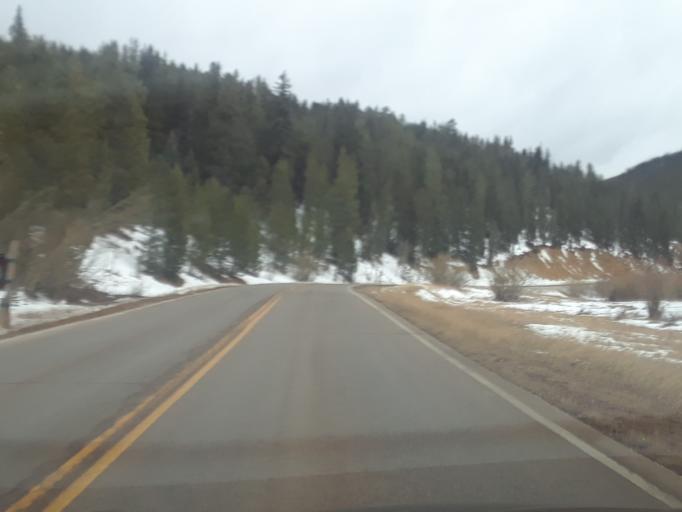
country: US
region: Colorado
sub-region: Boulder County
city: Coal Creek
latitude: 39.8285
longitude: -105.4102
